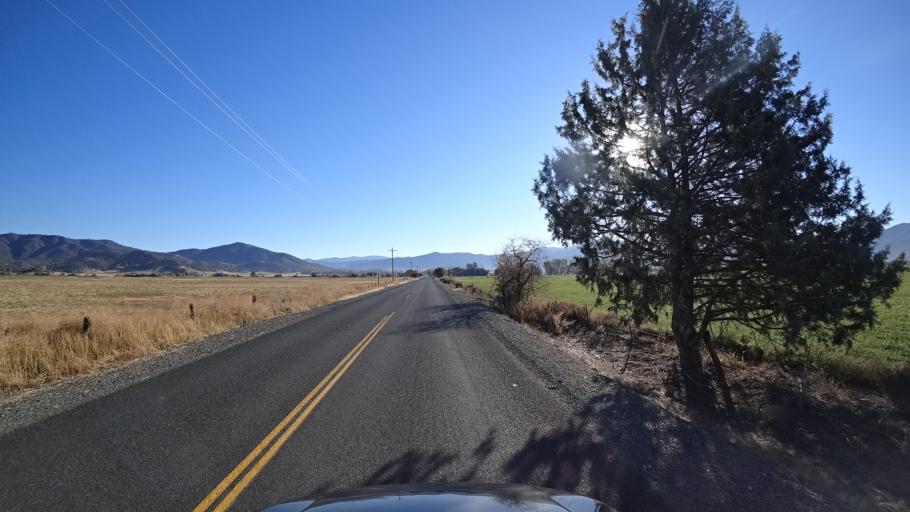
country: US
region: California
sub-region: Siskiyou County
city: Yreka
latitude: 41.5703
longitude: -122.8532
